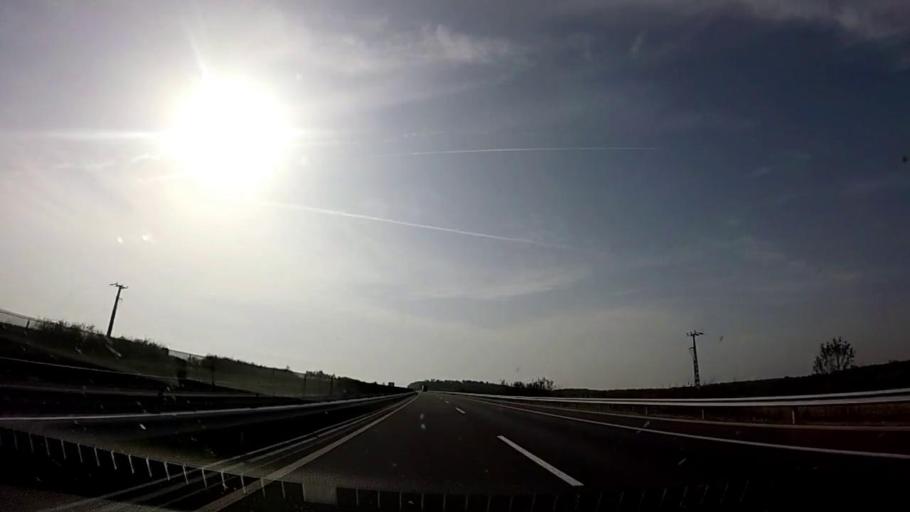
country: HU
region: Zala
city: Zalakomar
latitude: 46.5993
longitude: 17.2513
